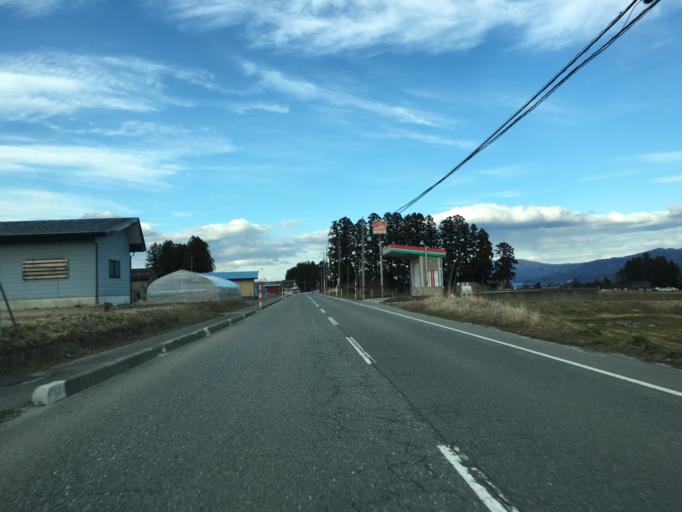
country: JP
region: Yamagata
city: Nagai
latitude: 38.1270
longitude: 140.0059
